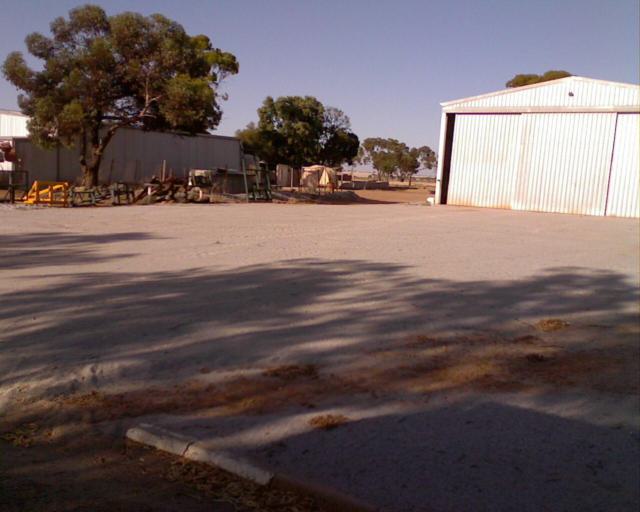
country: AU
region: Western Australia
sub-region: Merredin
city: Merredin
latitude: -31.1155
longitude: 117.7888
